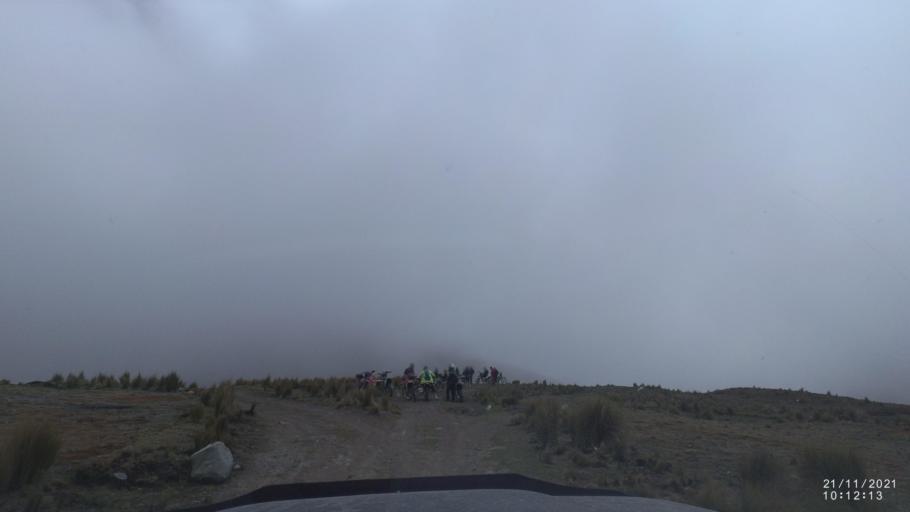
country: BO
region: Cochabamba
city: Cochabamba
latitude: -16.9921
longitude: -66.2678
